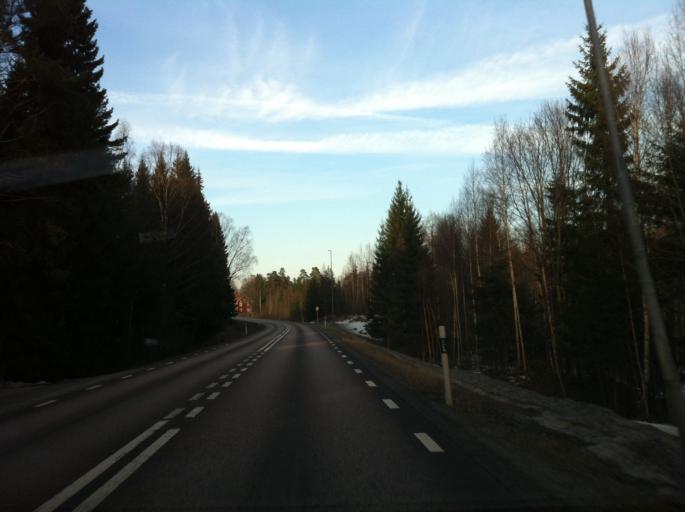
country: SE
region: Vaermland
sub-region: Filipstads Kommun
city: Lesjofors
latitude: 59.8474
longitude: 14.2592
